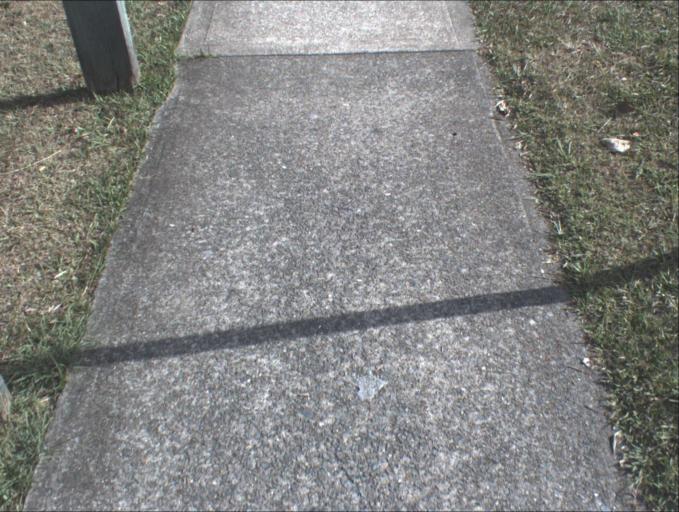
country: AU
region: Queensland
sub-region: Logan
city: Beenleigh
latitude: -27.7111
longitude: 153.2030
